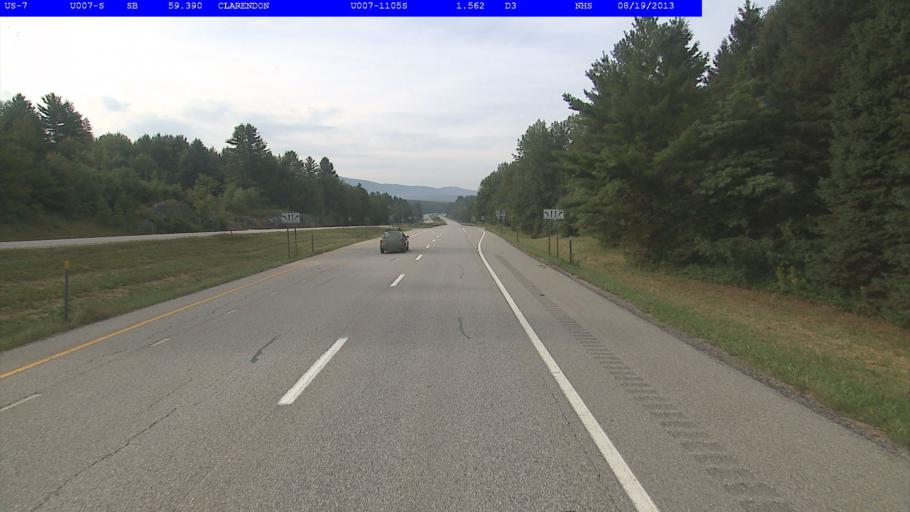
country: US
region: Vermont
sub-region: Rutland County
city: Rutland
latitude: 43.5174
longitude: -72.9679
